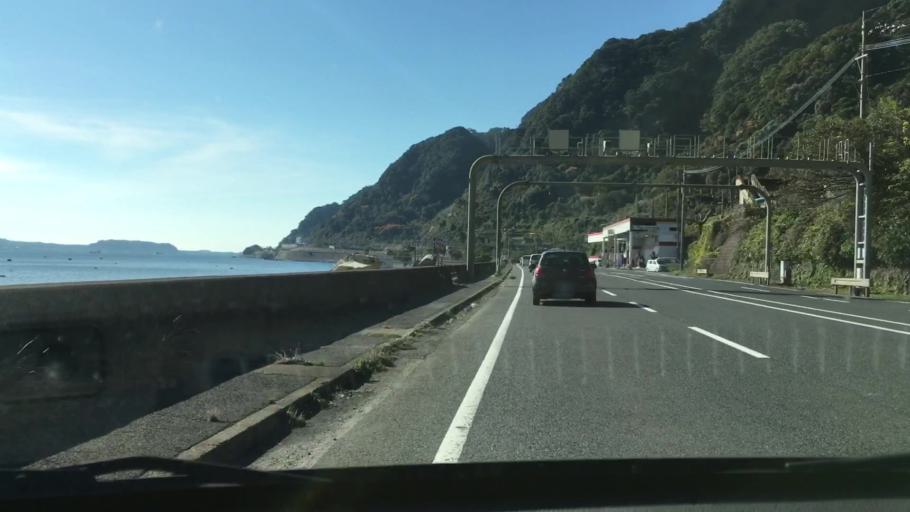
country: JP
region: Kagoshima
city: Kagoshima-shi
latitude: 31.6481
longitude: 130.6050
